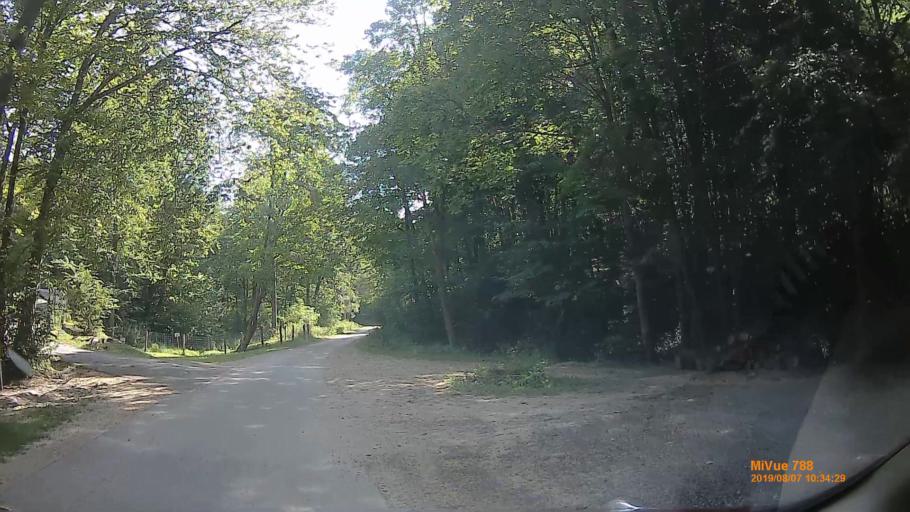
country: HU
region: Veszprem
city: Urkut
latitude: 47.0638
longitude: 17.5977
